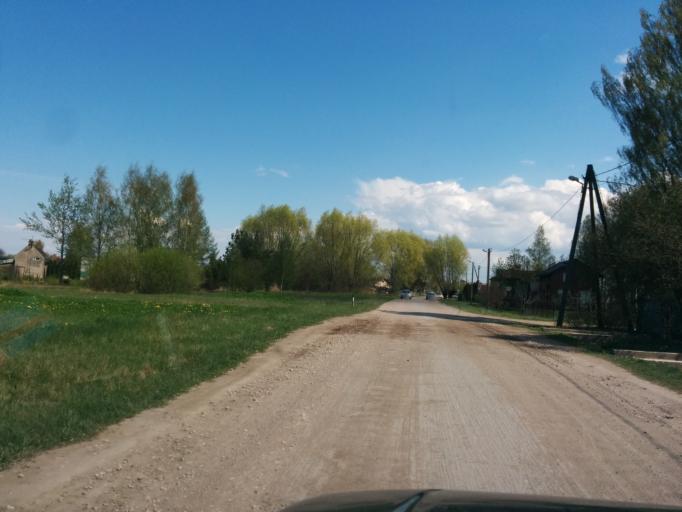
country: LV
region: Jelgava
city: Jelgava
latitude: 56.6300
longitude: 23.7098
